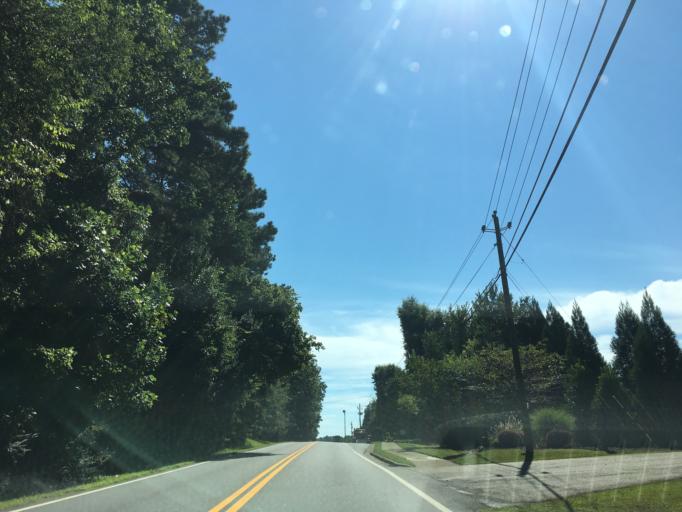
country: US
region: Georgia
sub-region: Fulton County
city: Milton
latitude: 34.1631
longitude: -84.3074
